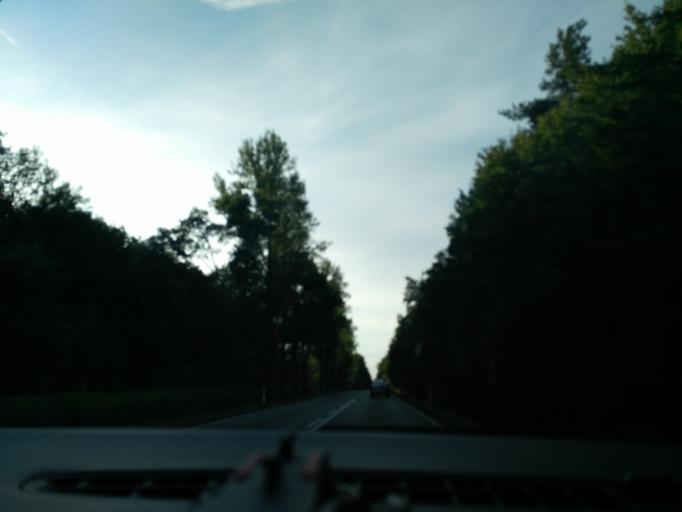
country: PL
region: Lublin Voivodeship
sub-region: Powiat krasnicki
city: Szastarka
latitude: 50.8476
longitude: 22.2917
